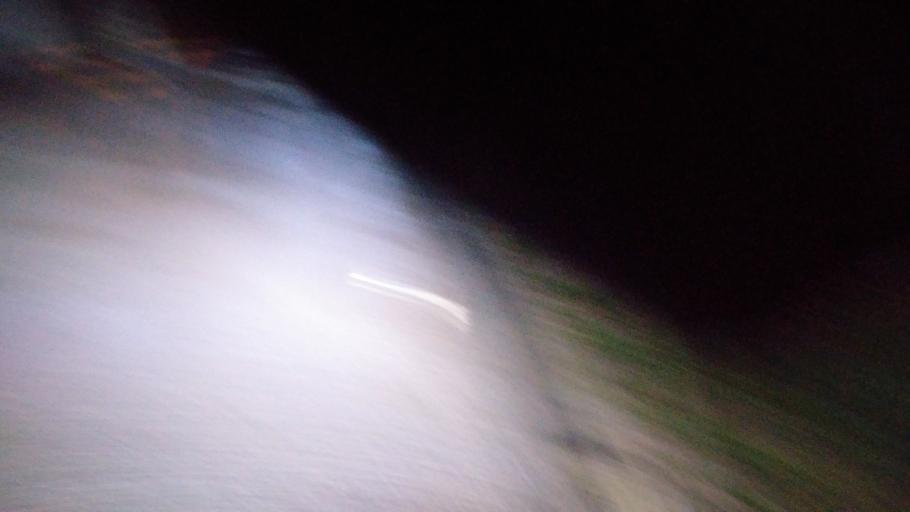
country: TR
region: Ankara
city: Ankara
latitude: 39.9349
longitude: 32.8269
